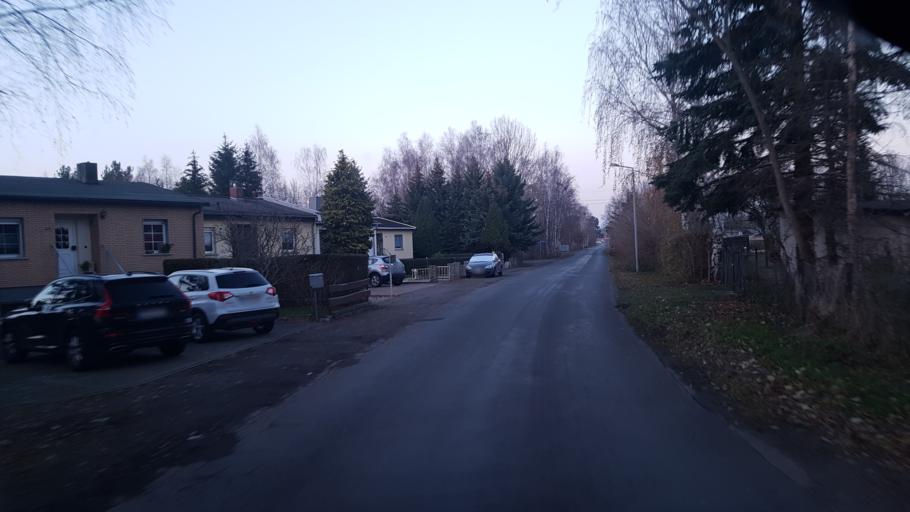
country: DE
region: Brandenburg
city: Lauchhammer
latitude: 51.5053
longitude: 13.7549
